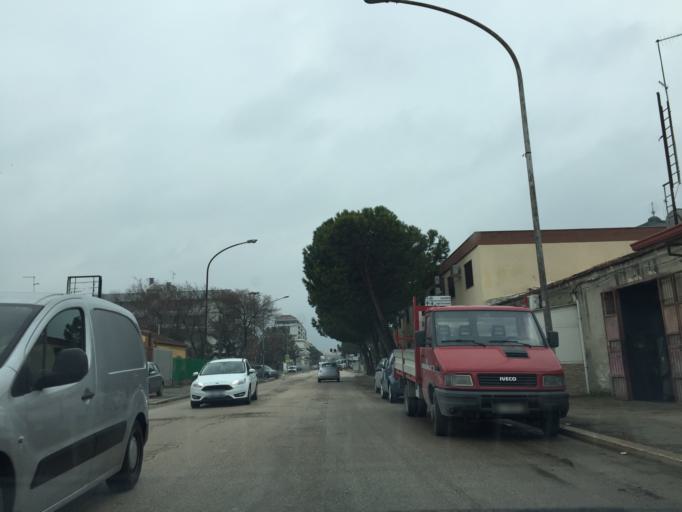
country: IT
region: Apulia
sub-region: Provincia di Foggia
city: Foggia
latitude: 41.4720
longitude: 15.5376
